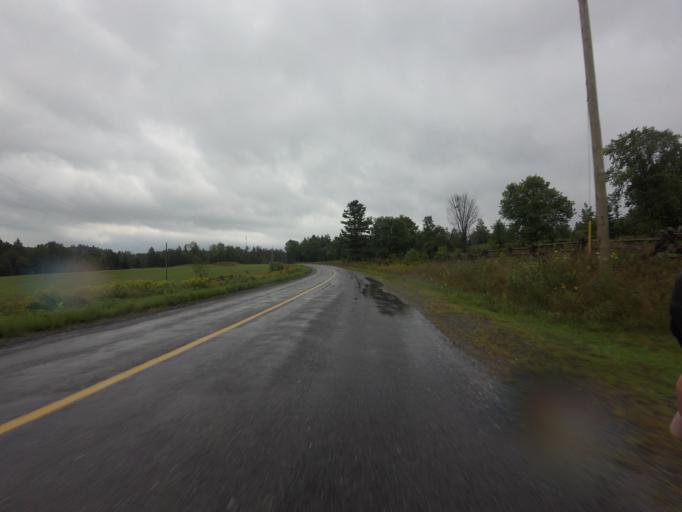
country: CA
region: Ontario
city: Renfrew
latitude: 45.0663
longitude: -76.6351
